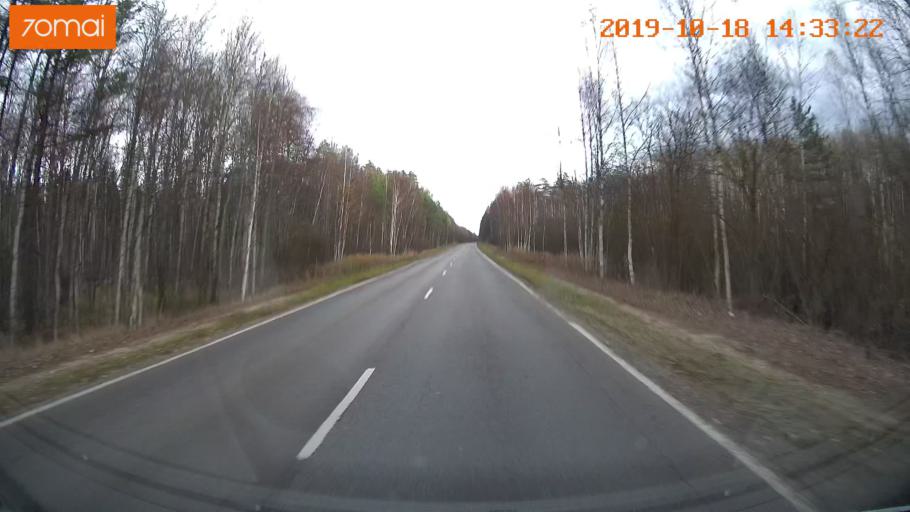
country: RU
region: Rjazan
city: Tuma
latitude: 55.2006
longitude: 40.5956
